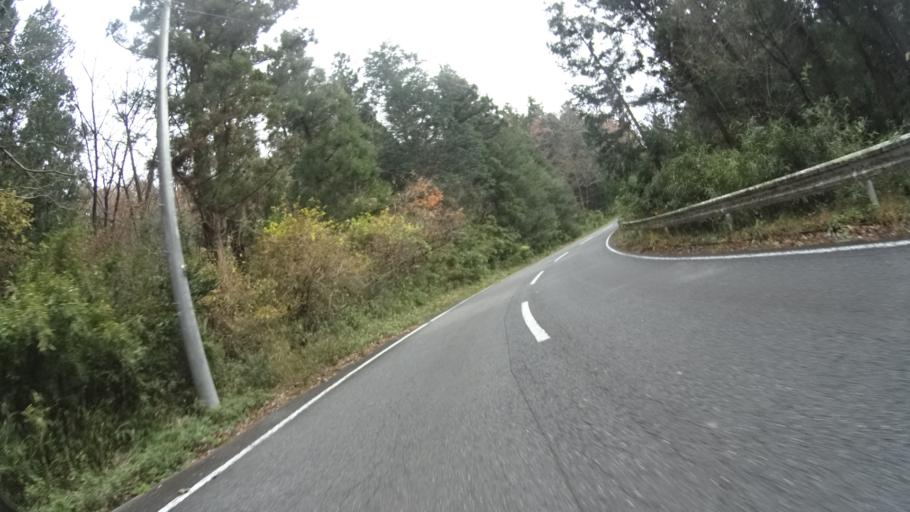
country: JP
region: Gunma
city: Omamacho-omama
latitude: 36.4772
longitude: 139.1590
